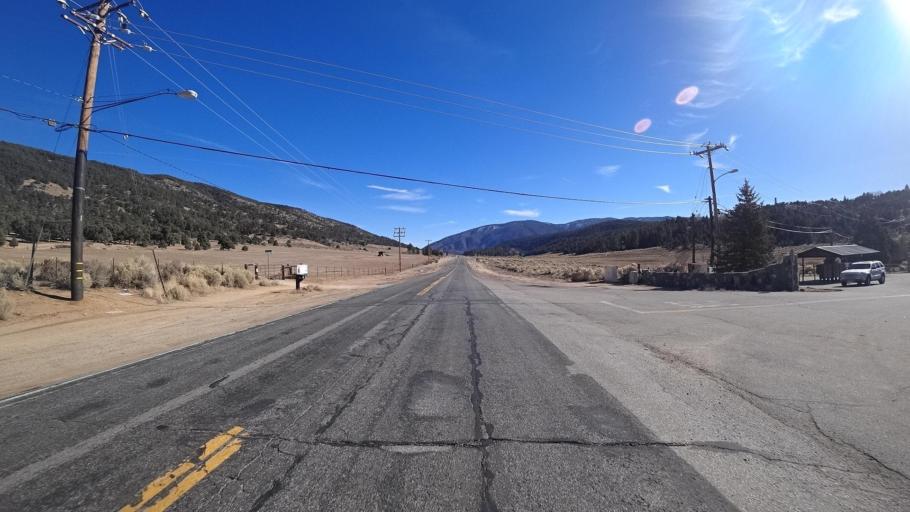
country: US
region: California
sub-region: Kern County
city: Frazier Park
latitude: 34.8358
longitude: -119.0406
